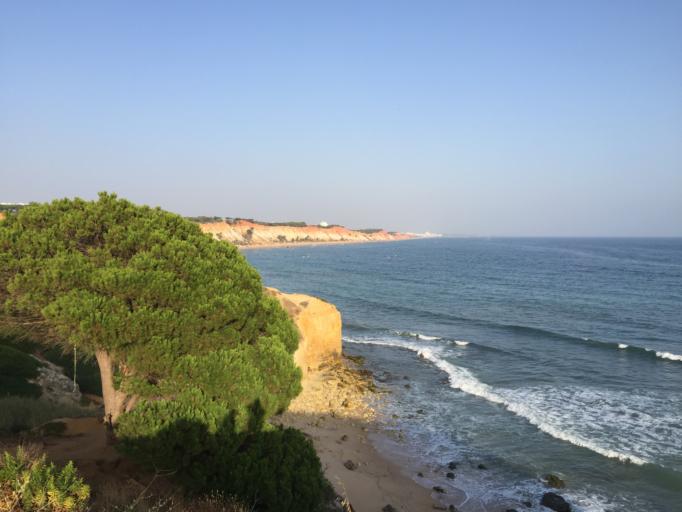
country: PT
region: Faro
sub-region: Loule
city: Boliqueime
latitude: 37.0898
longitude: -8.1886
